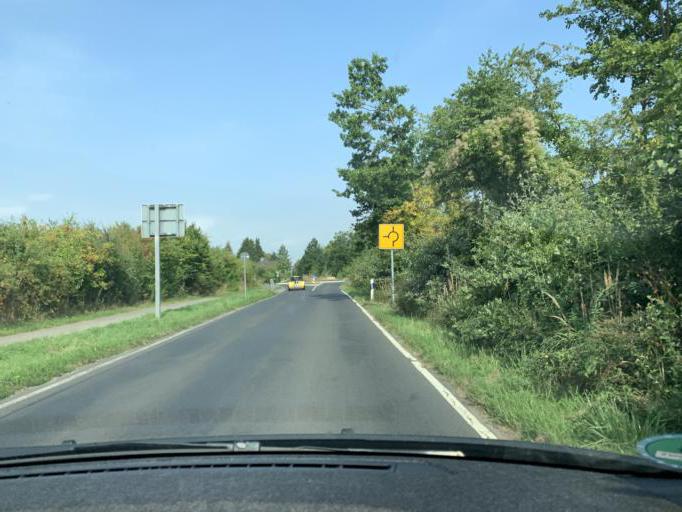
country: DE
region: North Rhine-Westphalia
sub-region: Regierungsbezirk Koln
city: Weilerswist
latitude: 50.8010
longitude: 6.8355
